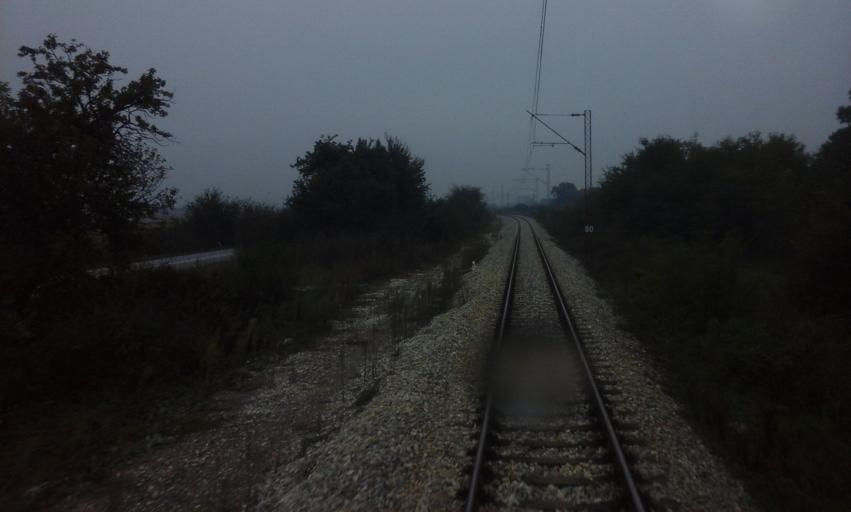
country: RS
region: Central Serbia
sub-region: Pomoravski Okrug
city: Paracin
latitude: 43.8883
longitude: 21.3829
